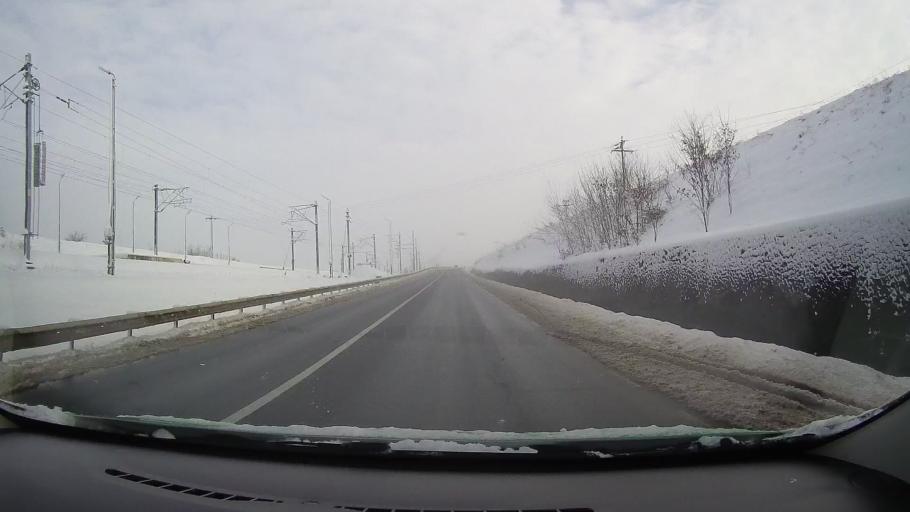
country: RO
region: Alba
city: Vurpar
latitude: 45.9854
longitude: 23.4884
